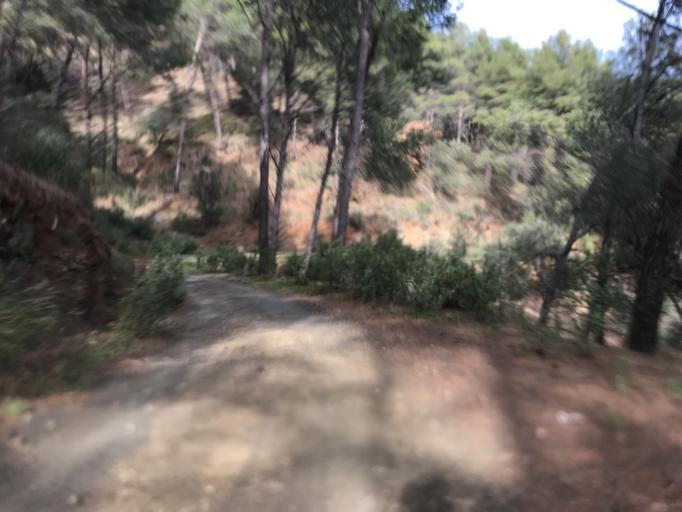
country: ES
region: Andalusia
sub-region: Provincia de Malaga
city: Malaga
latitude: 36.8048
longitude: -4.4005
